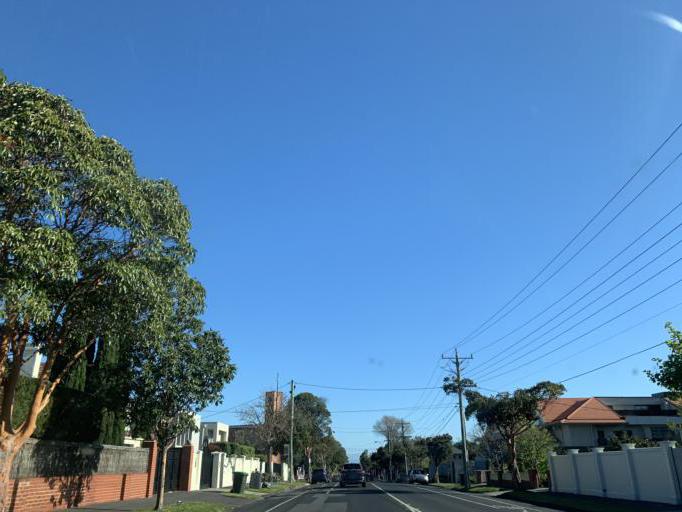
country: AU
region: Victoria
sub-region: Bayside
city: Hampton
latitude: -37.9252
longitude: 144.9947
